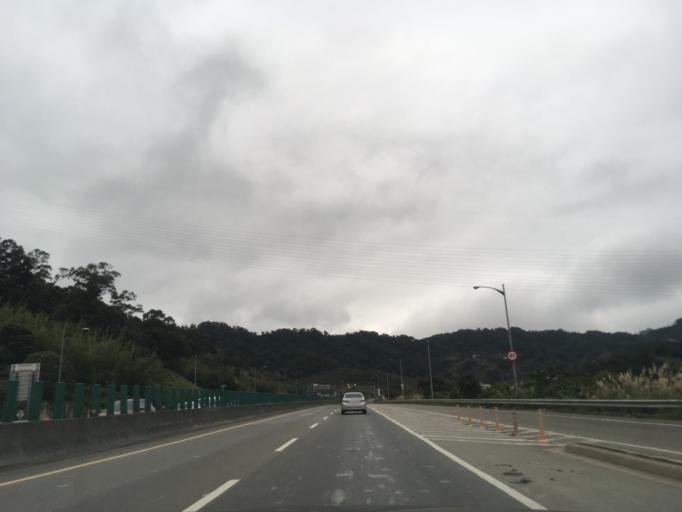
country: TW
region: Taipei
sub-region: Taipei
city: Banqiao
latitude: 25.1098
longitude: 121.4265
